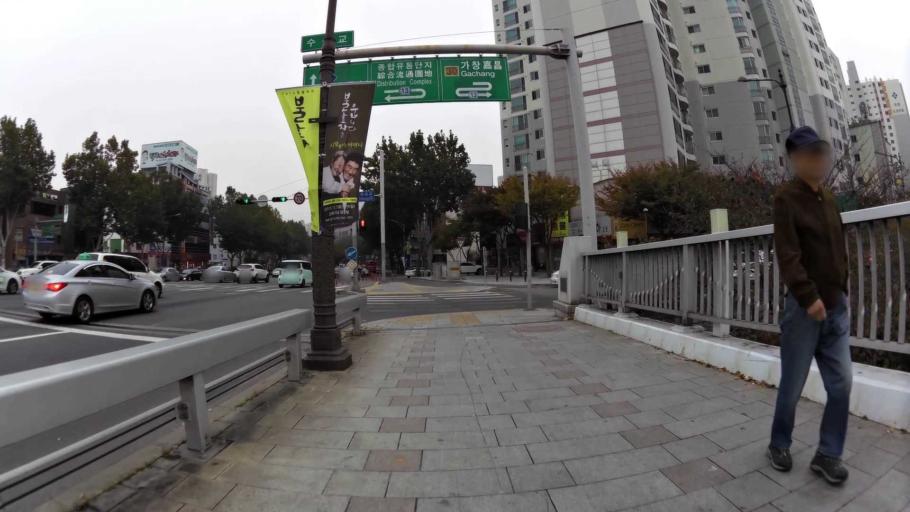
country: KR
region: Daegu
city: Daegu
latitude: 35.8609
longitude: 128.6092
